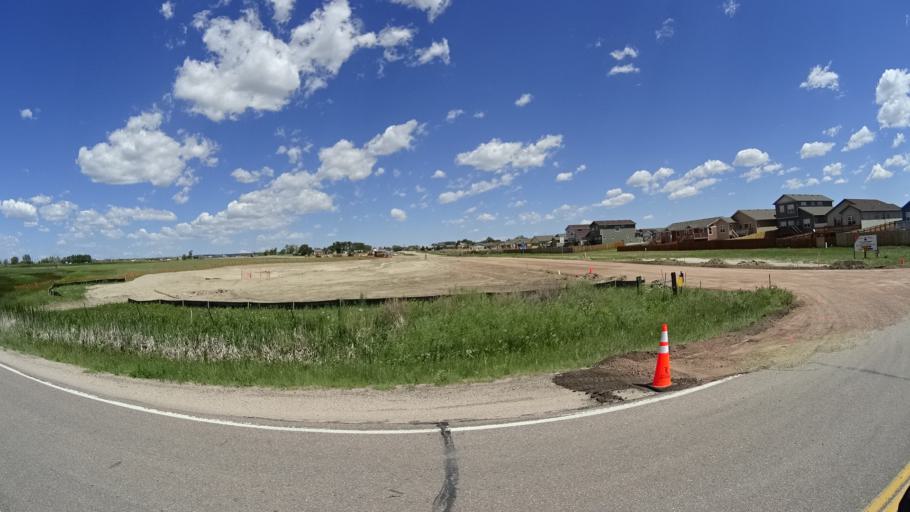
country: US
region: Colorado
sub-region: El Paso County
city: Cimarron Hills
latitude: 38.9262
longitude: -104.6078
